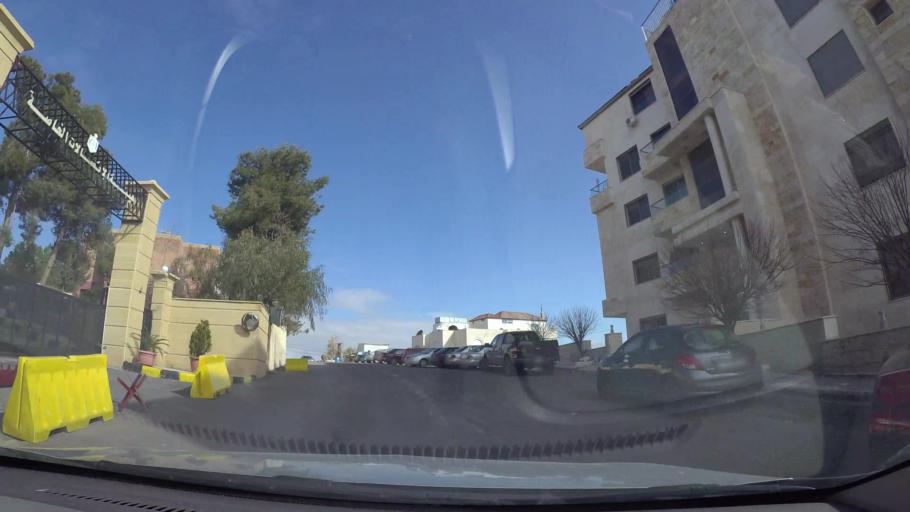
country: JO
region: Amman
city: Al Jubayhah
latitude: 32.0058
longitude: 35.8442
